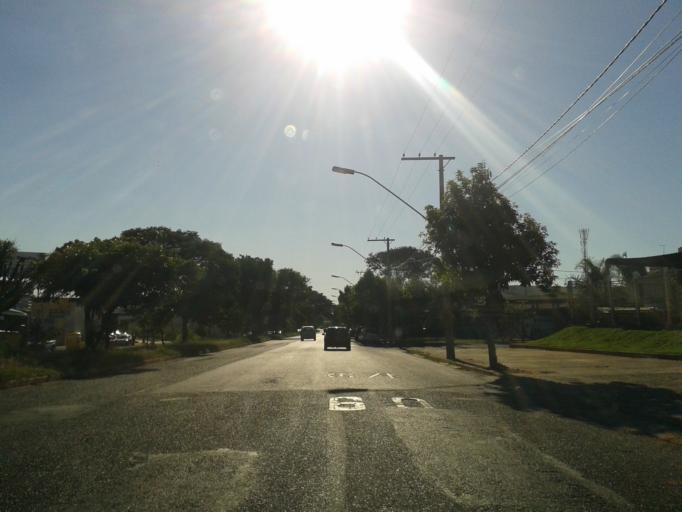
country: BR
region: Minas Gerais
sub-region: Uberlandia
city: Uberlandia
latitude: -18.9363
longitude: -48.2306
